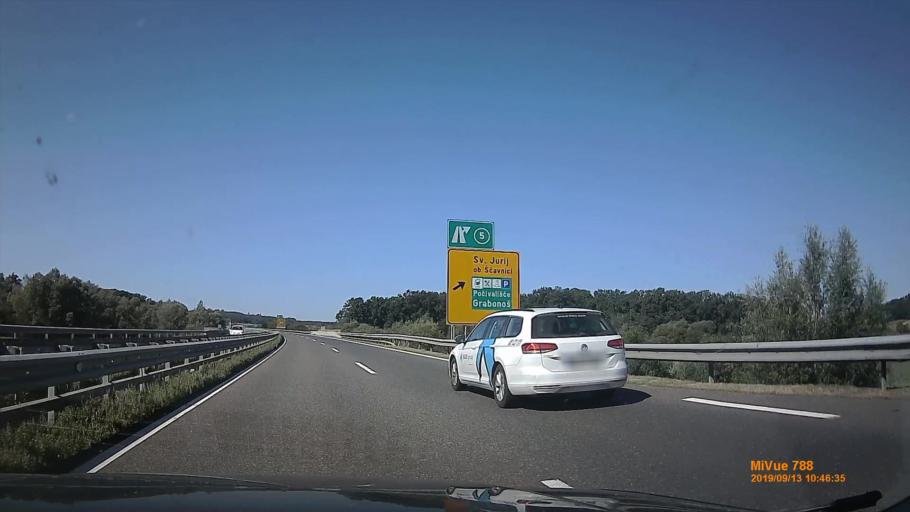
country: SI
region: Sveti Jurij
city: Sveti Jurij ob Scavnici
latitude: 46.5883
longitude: 16.0205
